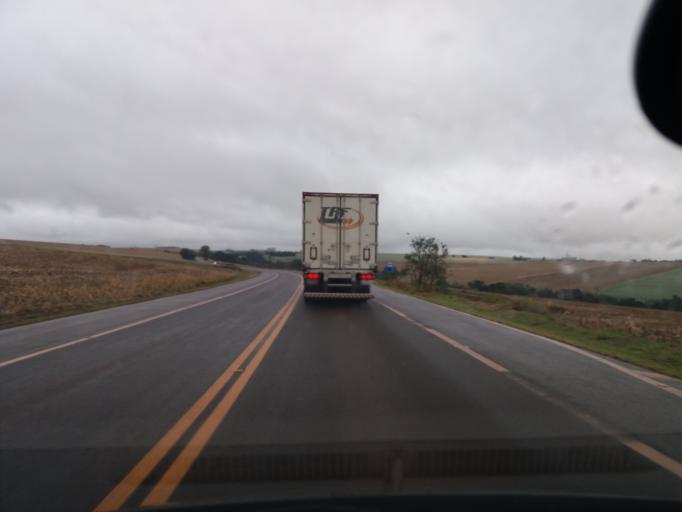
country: BR
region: Parana
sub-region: Campo Mourao
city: Campo Mourao
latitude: -24.3318
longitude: -52.6590
